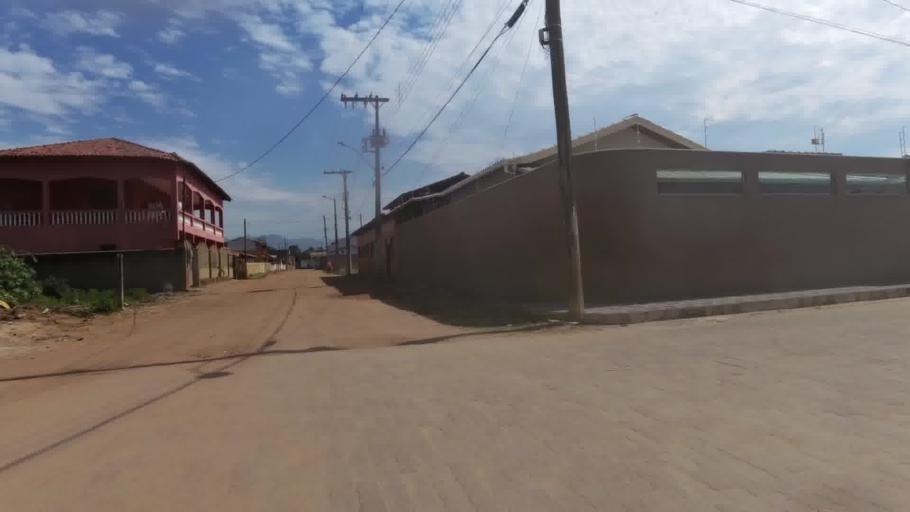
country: BR
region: Espirito Santo
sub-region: Piuma
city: Piuma
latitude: -20.8505
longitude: -40.7513
